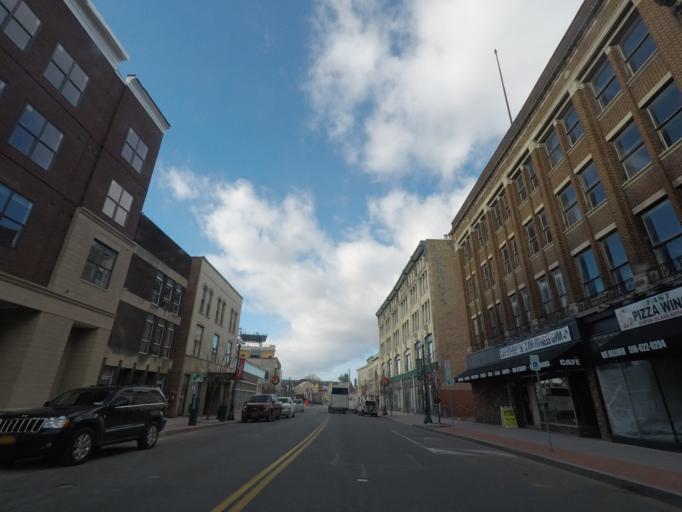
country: US
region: New York
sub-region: Schenectady County
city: Schenectady
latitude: 42.8146
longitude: -73.9448
